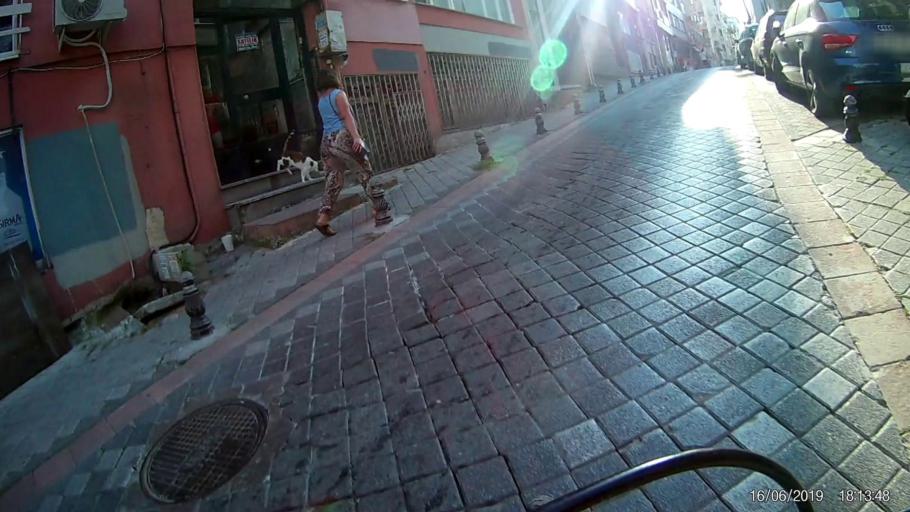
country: TR
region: Istanbul
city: UEskuedar
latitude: 40.9842
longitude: 29.0300
